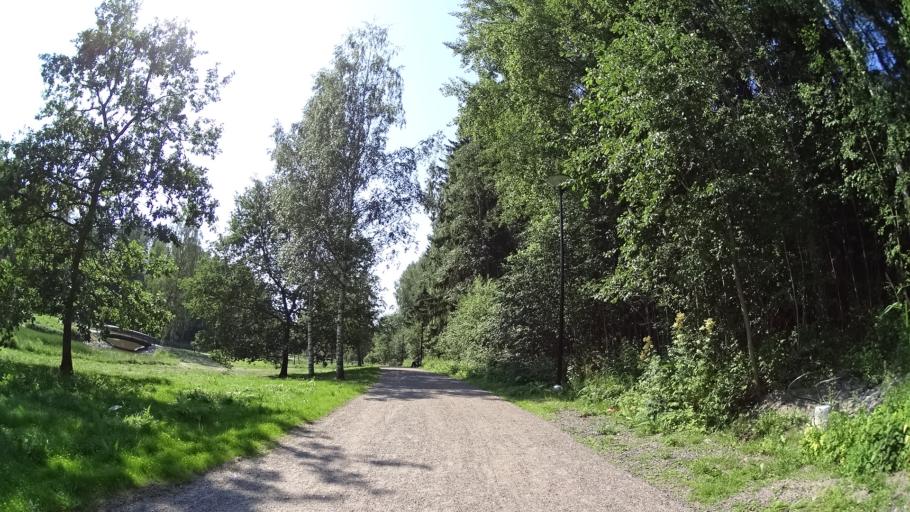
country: FI
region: Uusimaa
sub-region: Helsinki
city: Kerava
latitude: 60.3560
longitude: 25.0726
